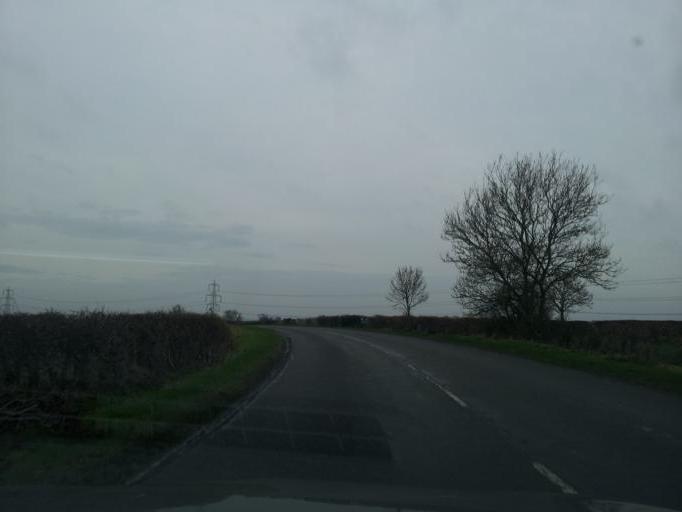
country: GB
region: England
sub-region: Lincolnshire
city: Long Bennington
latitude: 52.9895
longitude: -0.7674
